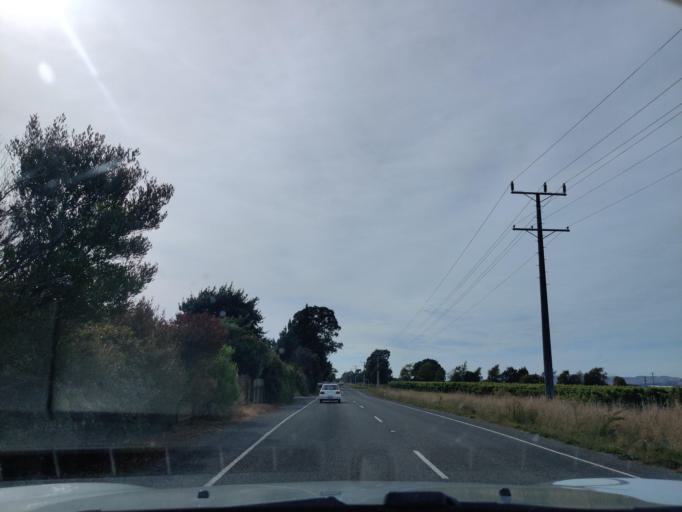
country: NZ
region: Marlborough
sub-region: Marlborough District
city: Blenheim
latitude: -41.5140
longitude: 173.8286
